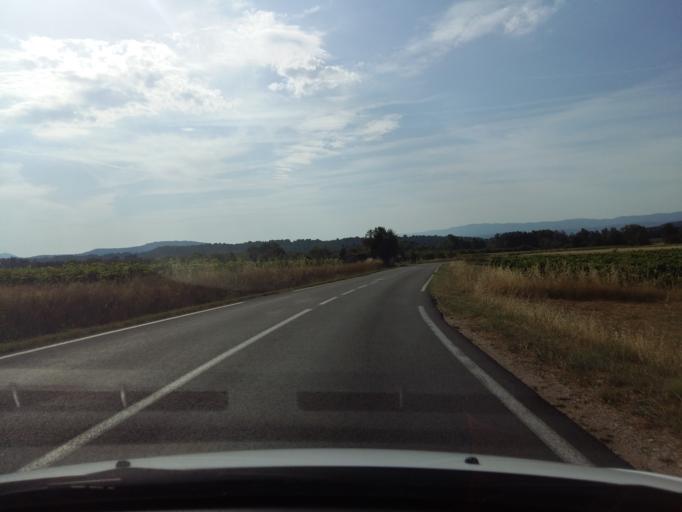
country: FR
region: Provence-Alpes-Cote d'Azur
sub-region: Departement du Vaucluse
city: Roussillon
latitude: 43.9270
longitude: 5.2958
